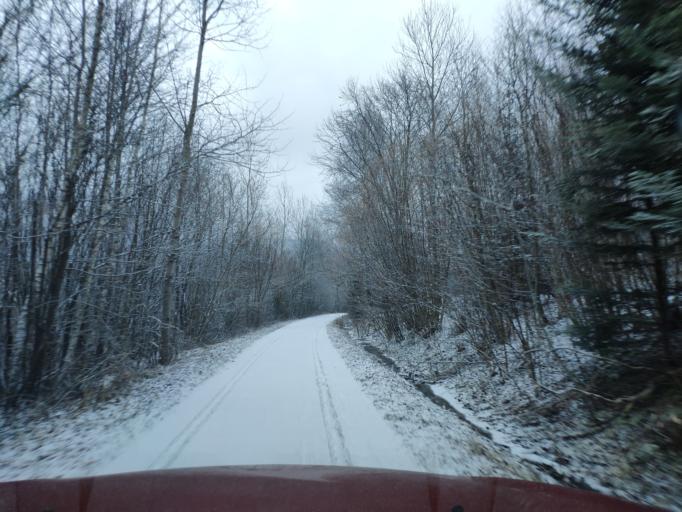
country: SK
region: Kosicky
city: Spisska Nova Ves
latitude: 48.8146
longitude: 20.5354
